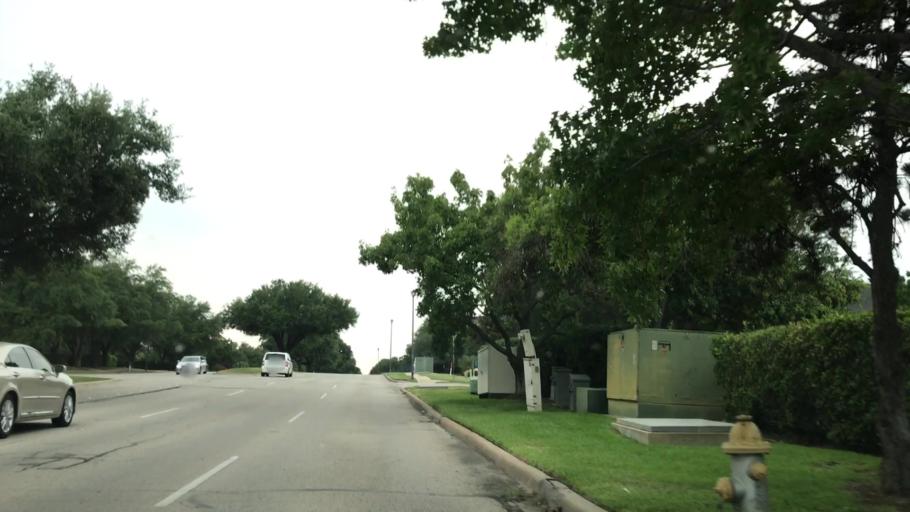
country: US
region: Texas
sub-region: Dallas County
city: Irving
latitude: 32.8851
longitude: -96.9667
